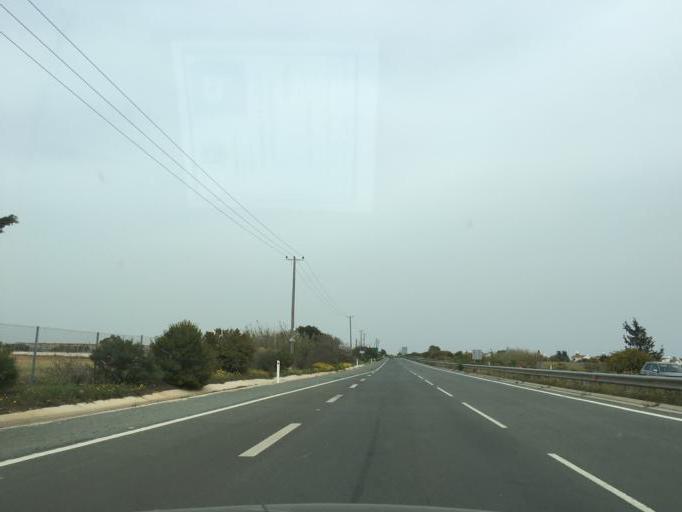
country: CY
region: Ammochostos
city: Liopetri
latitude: 34.9781
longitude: 33.9000
